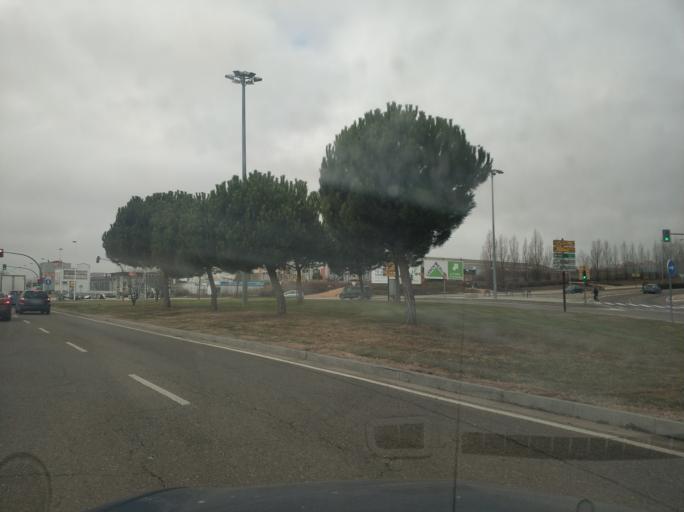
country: ES
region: Castille and Leon
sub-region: Provincia de Valladolid
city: Zaratan
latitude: 41.6277
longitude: -4.7585
